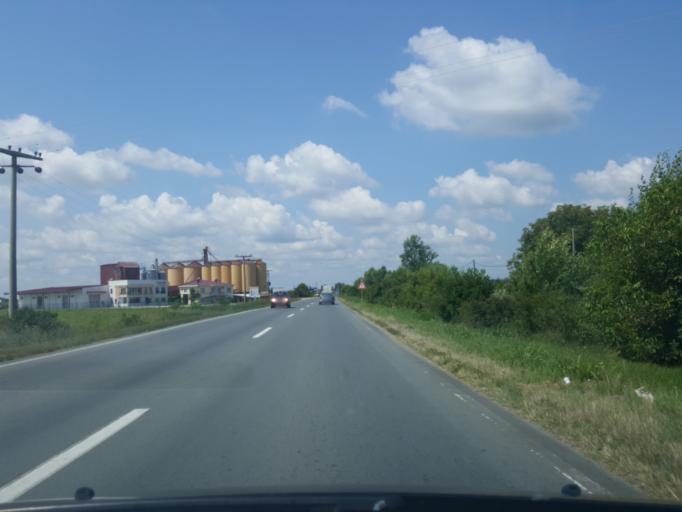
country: RS
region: Autonomna Pokrajina Vojvodina
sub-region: Sremski Okrug
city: Sremska Mitrovica
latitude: 44.9517
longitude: 19.6172
